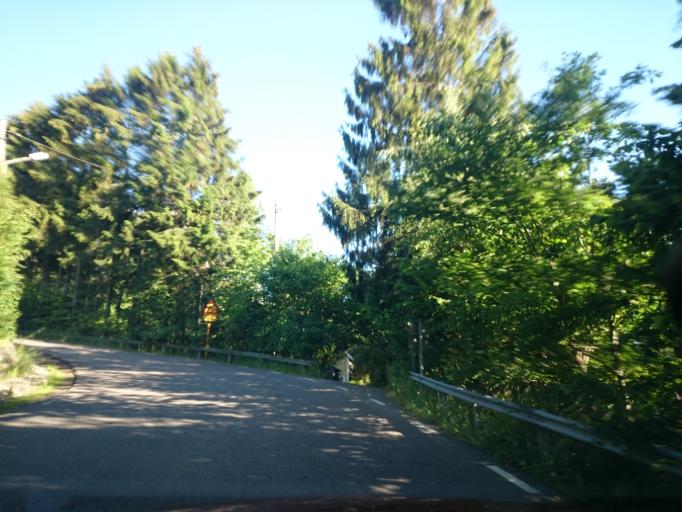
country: SE
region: Vaestra Goetaland
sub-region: Lerums Kommun
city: Stenkullen
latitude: 57.7865
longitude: 12.3141
